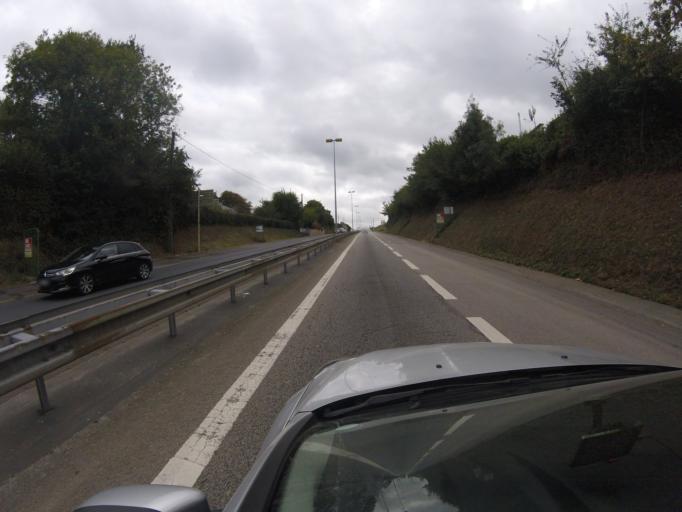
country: FR
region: Lower Normandy
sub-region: Departement de la Manche
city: La Glacerie
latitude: 49.6115
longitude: -1.6009
